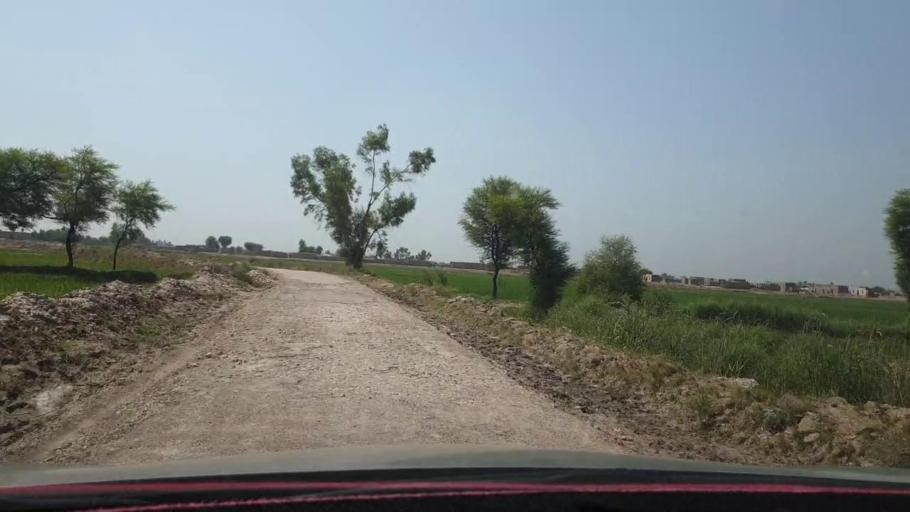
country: PK
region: Sindh
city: Warah
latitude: 27.4896
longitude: 67.8202
